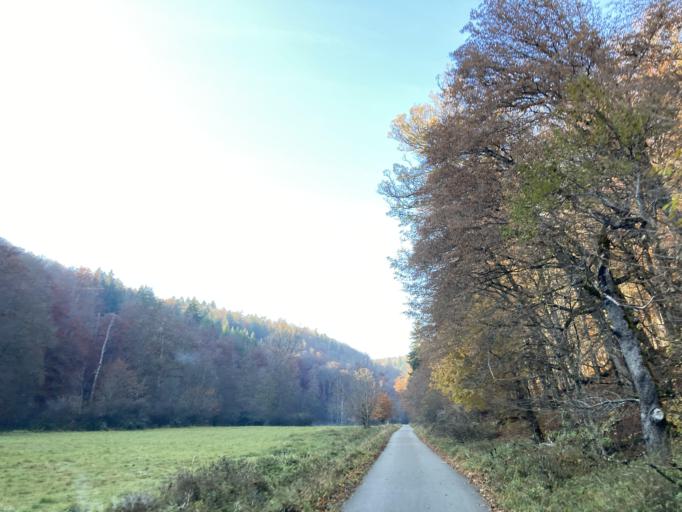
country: DE
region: Baden-Wuerttemberg
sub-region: Tuebingen Region
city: Tuebingen
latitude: 48.5617
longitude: 9.0394
